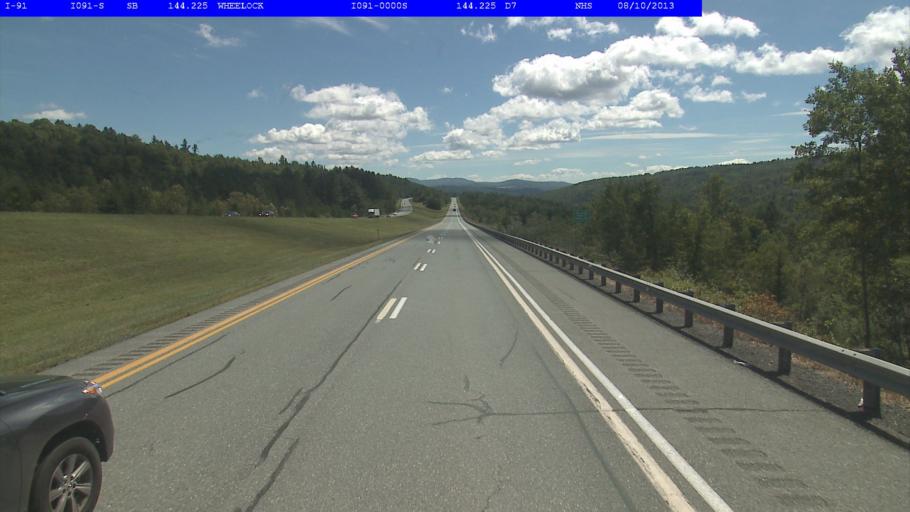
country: US
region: Vermont
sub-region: Caledonia County
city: Lyndonville
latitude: 44.5923
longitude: -72.0892
